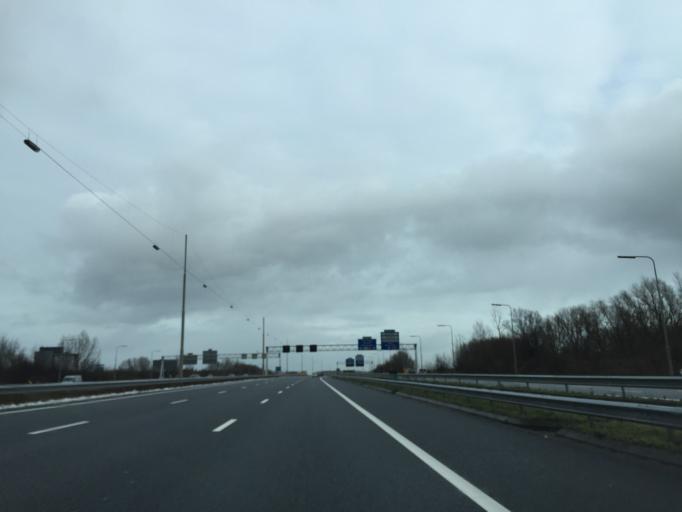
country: NL
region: South Holland
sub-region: Gemeente Rijswijk
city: Rijswijk
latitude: 52.0392
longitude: 4.3414
